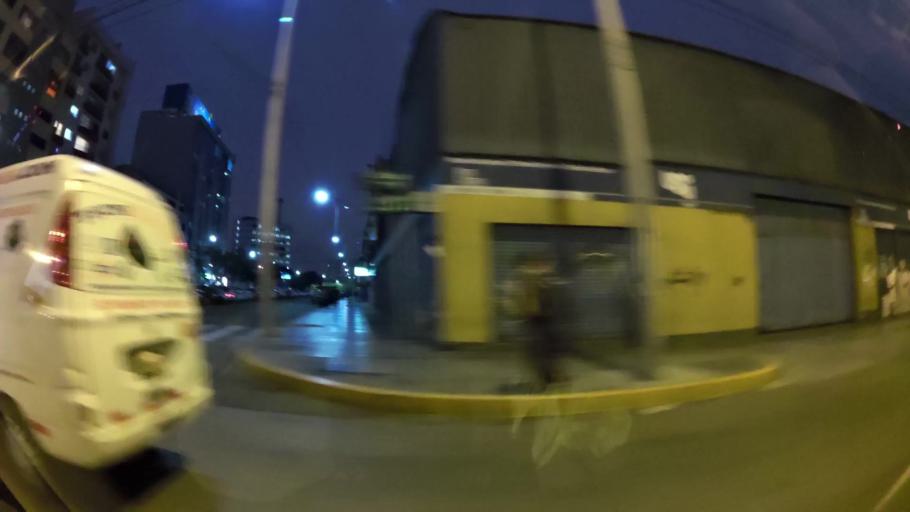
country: PE
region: Callao
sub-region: Callao
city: Callao
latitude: -12.0753
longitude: -77.0923
